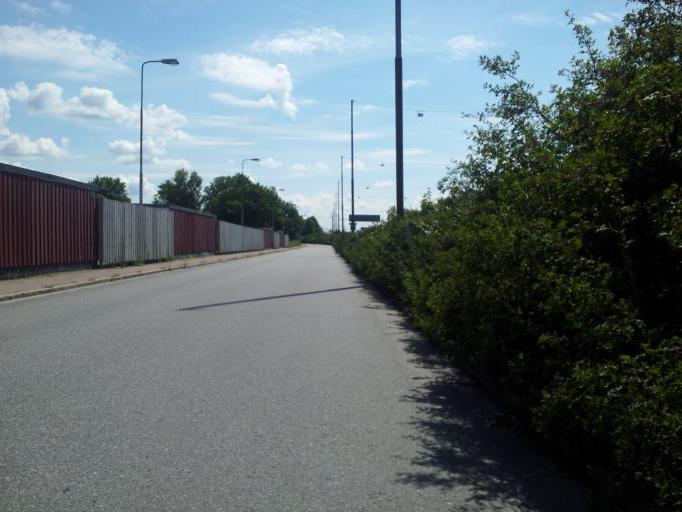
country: SE
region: Uppsala
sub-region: Uppsala Kommun
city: Uppsala
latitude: 59.8716
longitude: 17.6528
